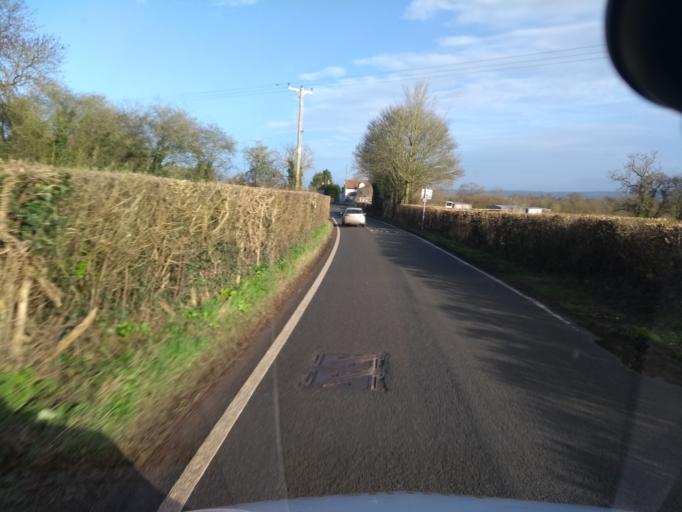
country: GB
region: England
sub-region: Somerset
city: Wedmore
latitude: 51.2183
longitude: -2.7883
